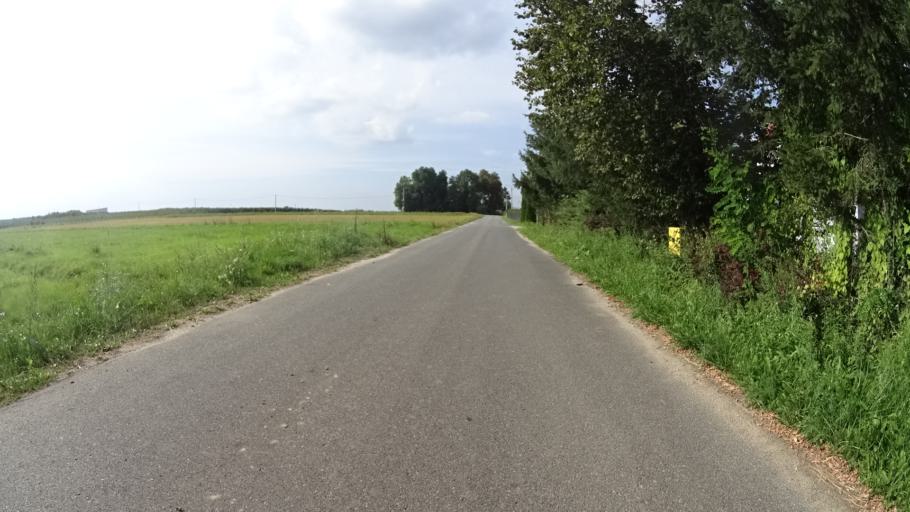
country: PL
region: Masovian Voivodeship
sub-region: Powiat grojecki
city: Goszczyn
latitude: 51.7085
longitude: 20.8419
